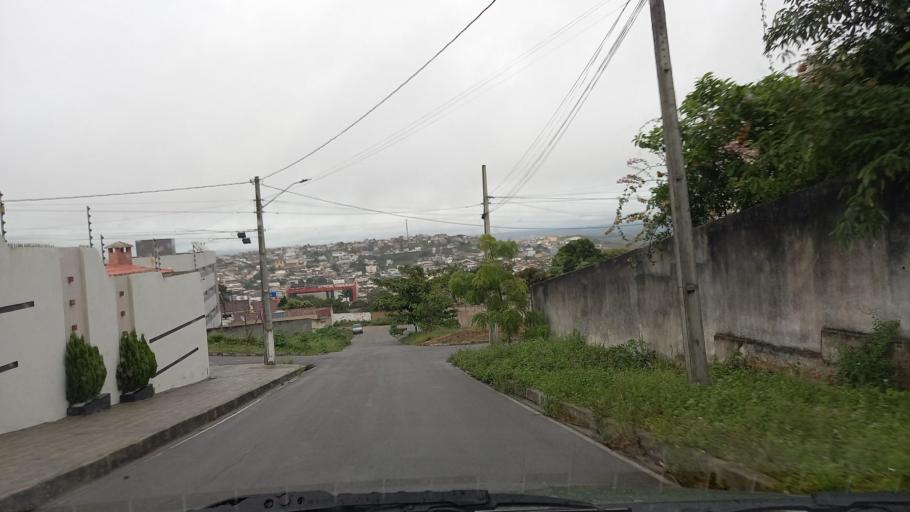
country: BR
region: Pernambuco
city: Garanhuns
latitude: -8.8857
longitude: -36.4962
